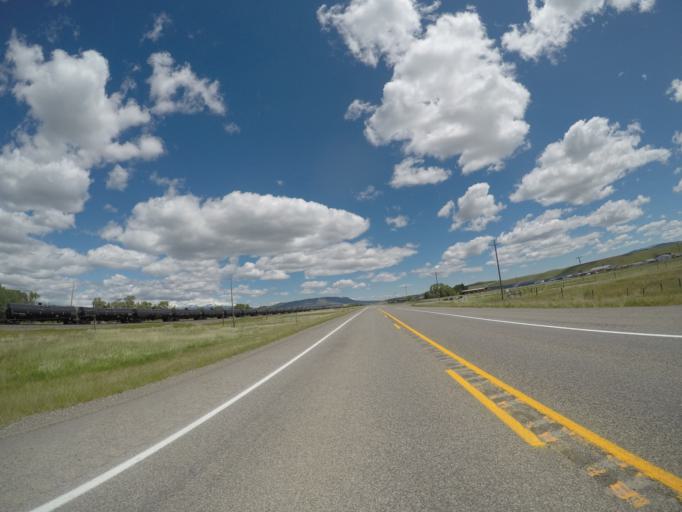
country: US
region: Montana
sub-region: Park County
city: Livingston
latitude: 45.6811
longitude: -110.5211
